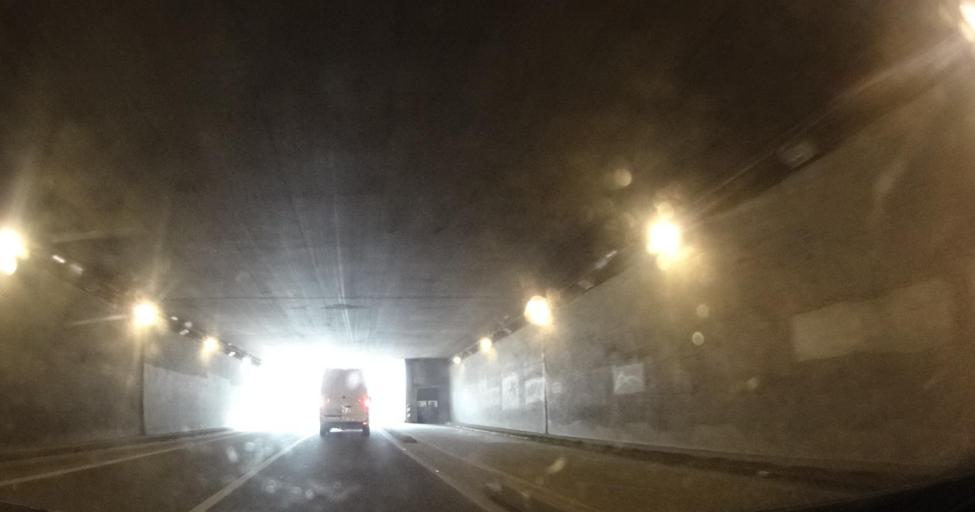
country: FR
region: Pays de la Loire
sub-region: Departement de la Loire-Atlantique
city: Nantes
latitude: 47.2178
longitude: -1.5427
